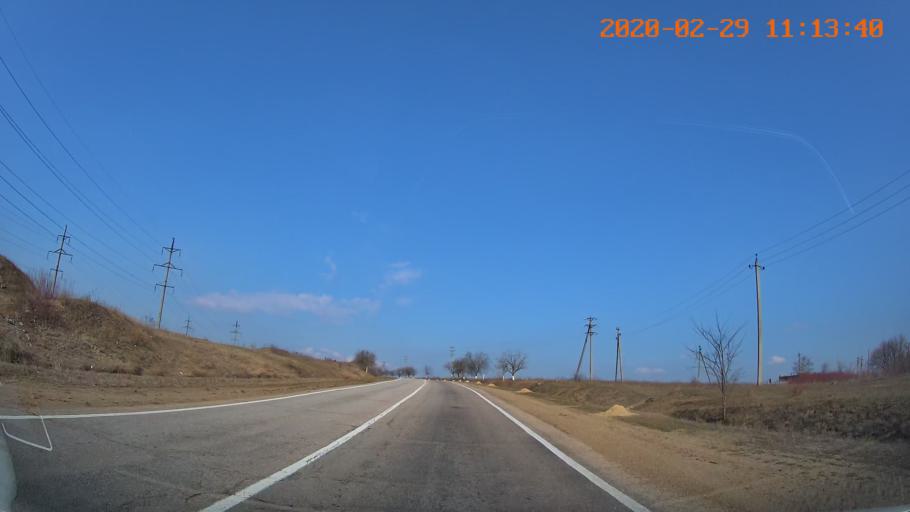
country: MD
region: Telenesti
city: Dubasari
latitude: 47.2744
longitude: 29.1804
